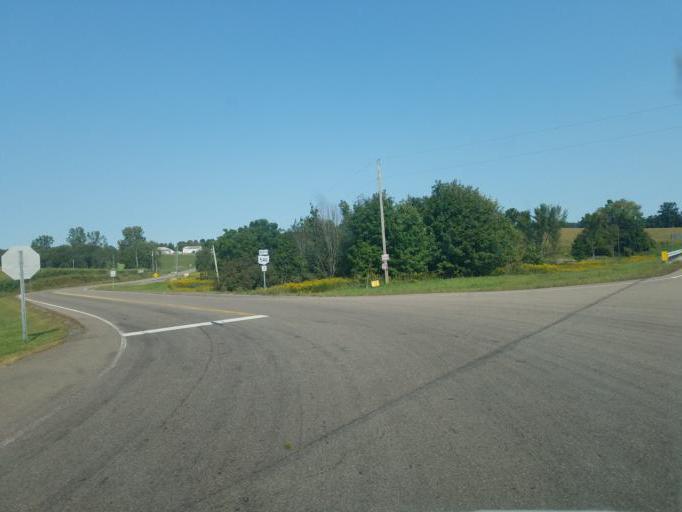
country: US
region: Ohio
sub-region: Knox County
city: Fredericktown
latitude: 40.5233
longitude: -82.5482
